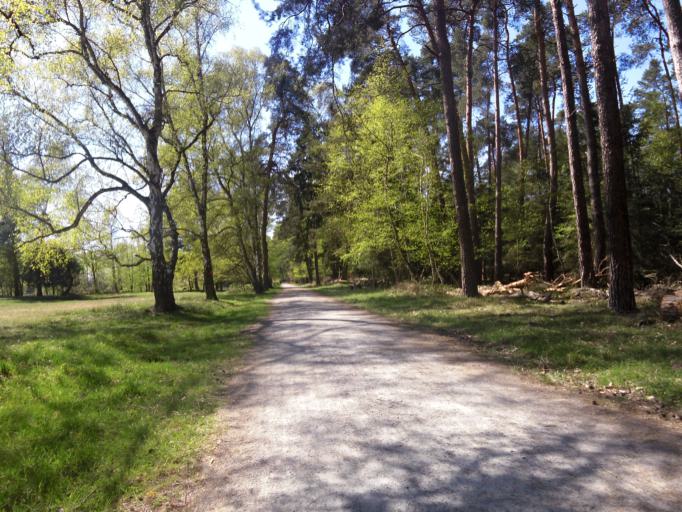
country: DE
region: Hesse
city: Morfelden-Walldorf
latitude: 50.0035
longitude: 8.5560
